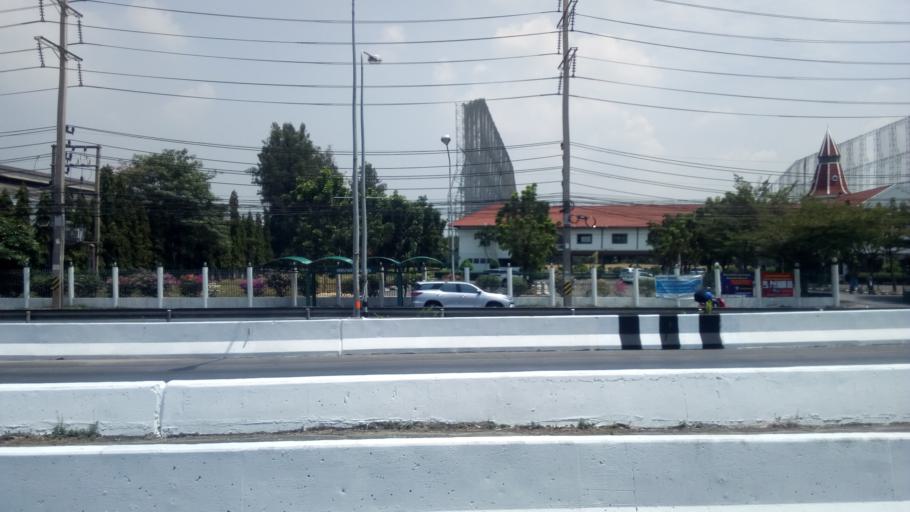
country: TH
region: Phra Nakhon Si Ayutthaya
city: Ban Bang Kadi Pathum Thani
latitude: 13.9841
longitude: 100.5901
